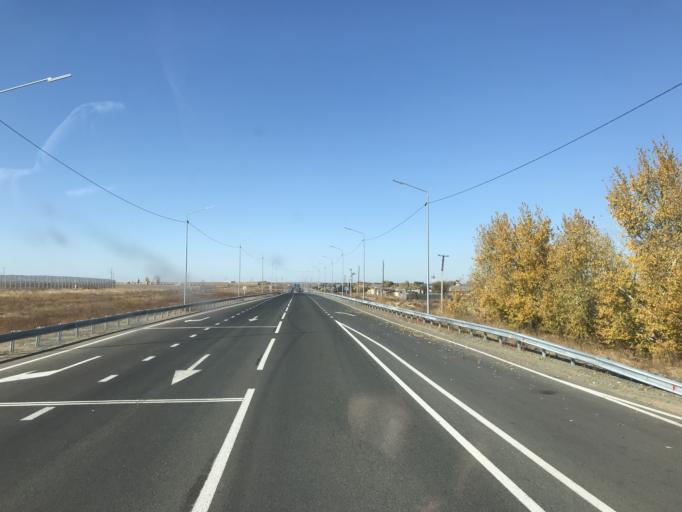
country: RU
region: Altai Krai
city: Malinovoye Ozero
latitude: 50.8802
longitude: 79.4764
